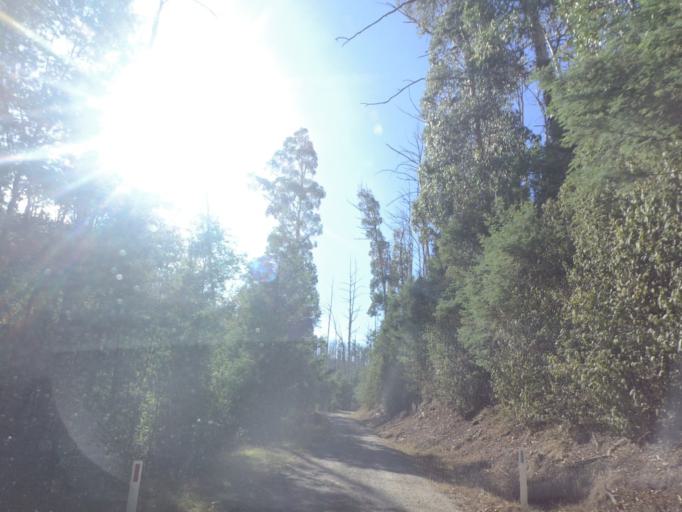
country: AU
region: Victoria
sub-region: Yarra Ranges
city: Millgrove
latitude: -37.4983
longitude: 145.8032
